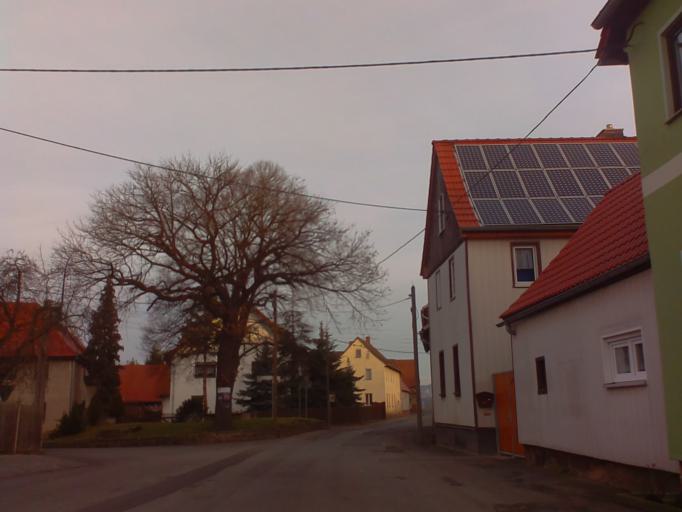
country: DE
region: Thuringia
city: Schops
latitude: 50.8324
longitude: 11.6057
